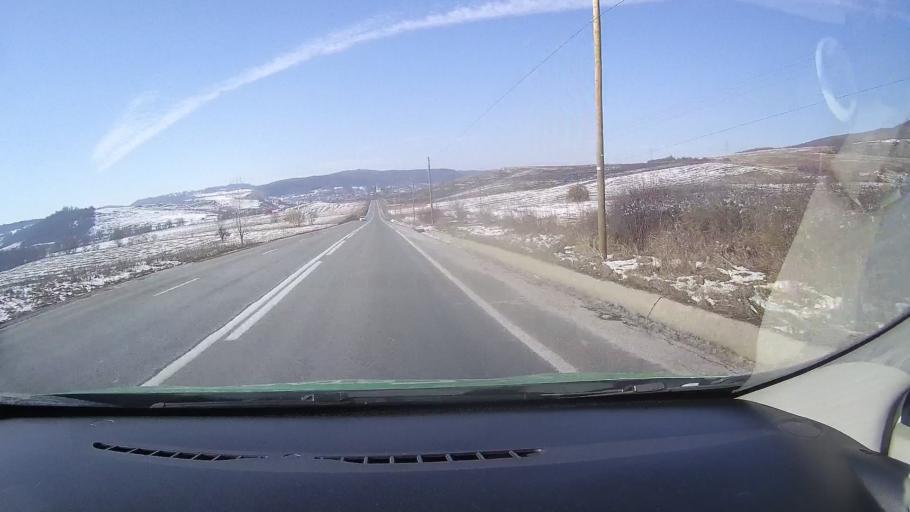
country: RO
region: Brasov
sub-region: Comuna Bunesti
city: Bunesti
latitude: 46.1142
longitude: 25.0411
